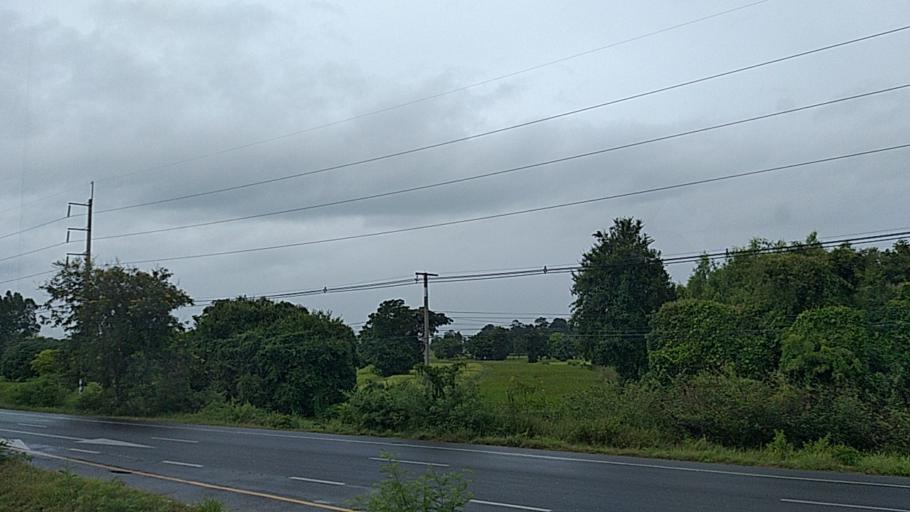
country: TH
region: Maha Sarakham
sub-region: Amphoe Borabue
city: Borabue
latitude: 16.0722
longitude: 103.1507
